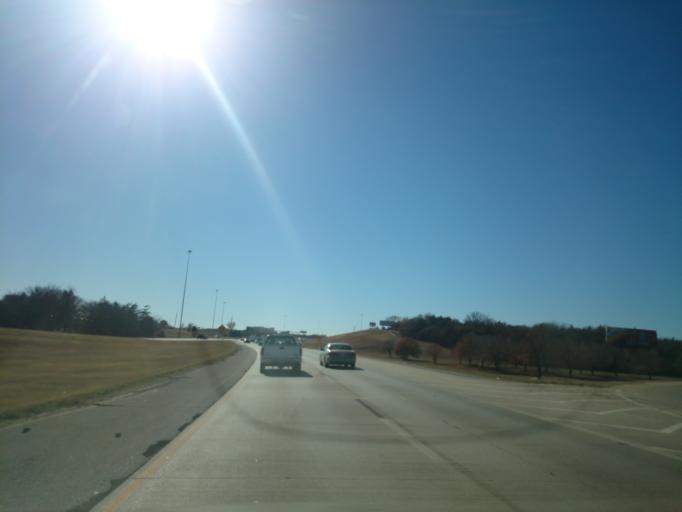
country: US
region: Oklahoma
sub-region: Oklahoma County
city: Edmond
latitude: 35.5999
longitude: -97.4309
